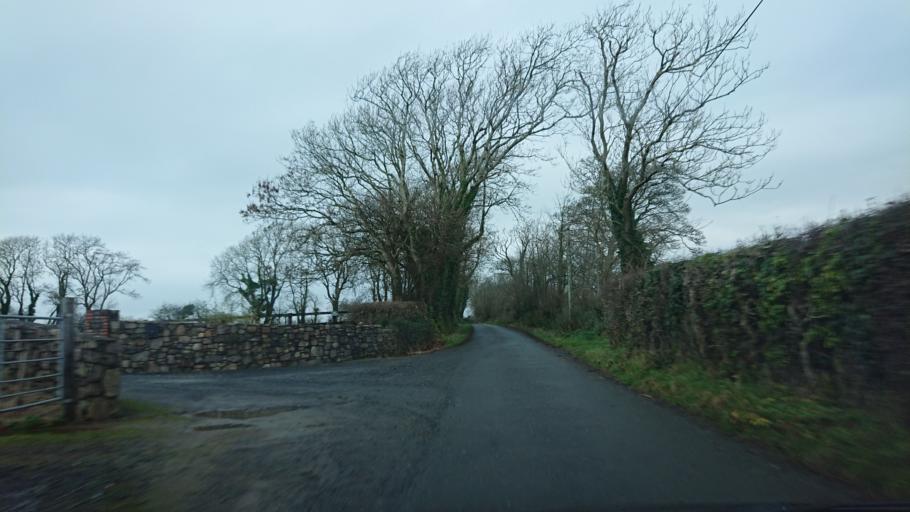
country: IE
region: Munster
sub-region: Waterford
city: Dunmore East
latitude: 52.2029
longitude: -7.0130
